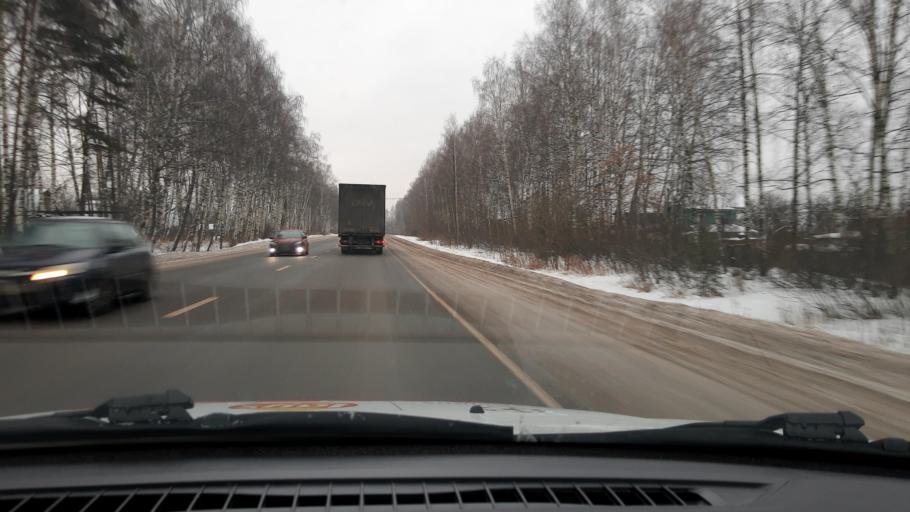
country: RU
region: Nizjnij Novgorod
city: Sitniki
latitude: 56.4588
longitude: 44.0276
